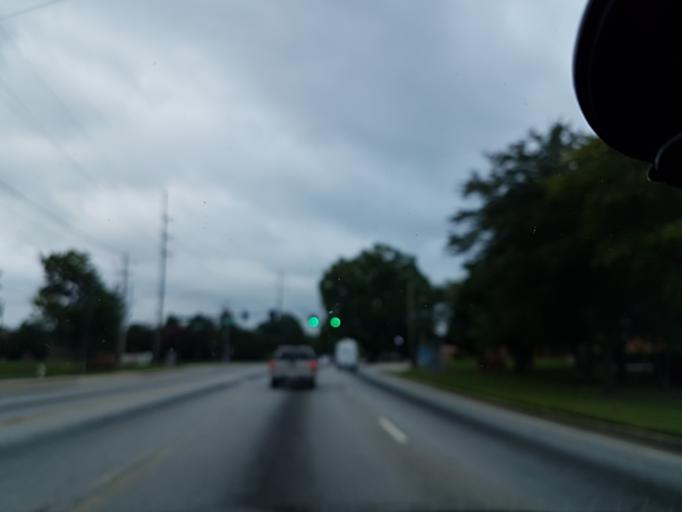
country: US
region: Georgia
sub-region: DeKalb County
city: Tucker
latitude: 33.8297
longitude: -84.1965
